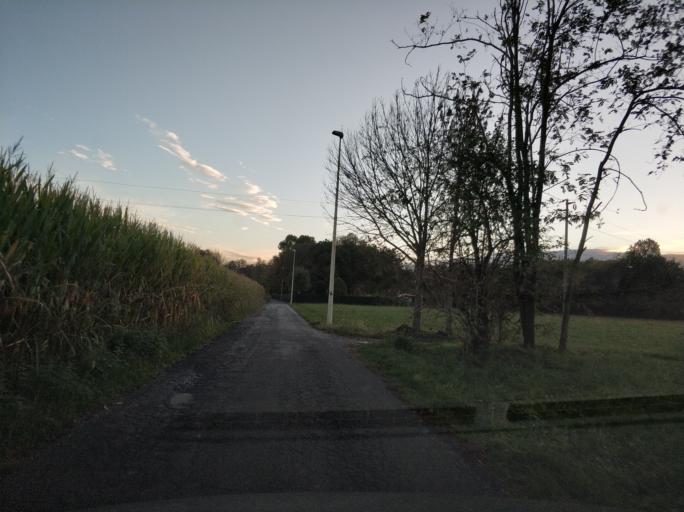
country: IT
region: Piedmont
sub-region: Provincia di Torino
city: Cirie
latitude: 45.2207
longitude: 7.5867
